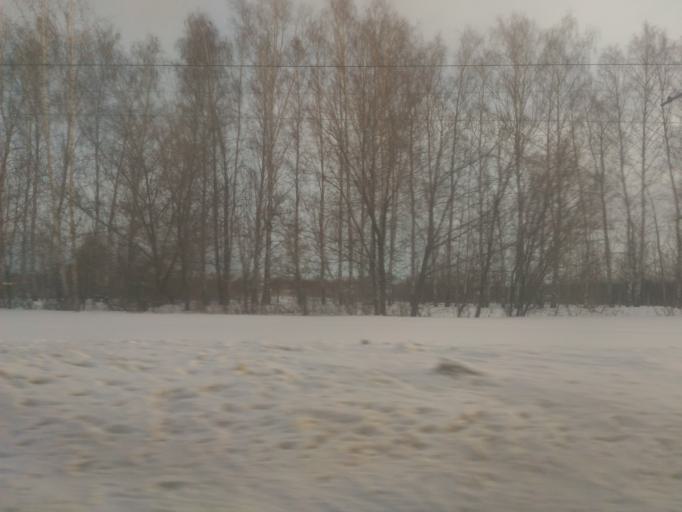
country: RU
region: Ulyanovsk
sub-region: Ulyanovskiy Rayon
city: Ulyanovsk
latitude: 54.3651
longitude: 48.3272
